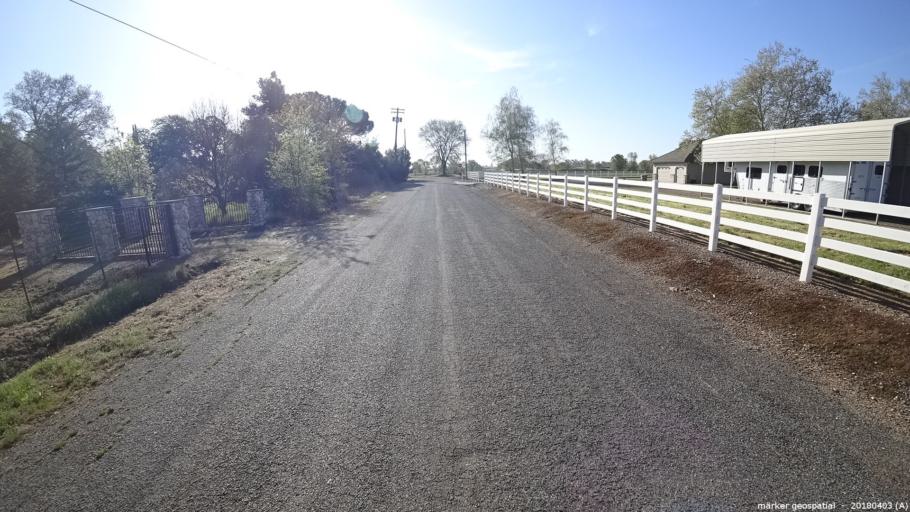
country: US
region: California
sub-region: Sacramento County
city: Wilton
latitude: 38.4355
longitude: -121.1940
